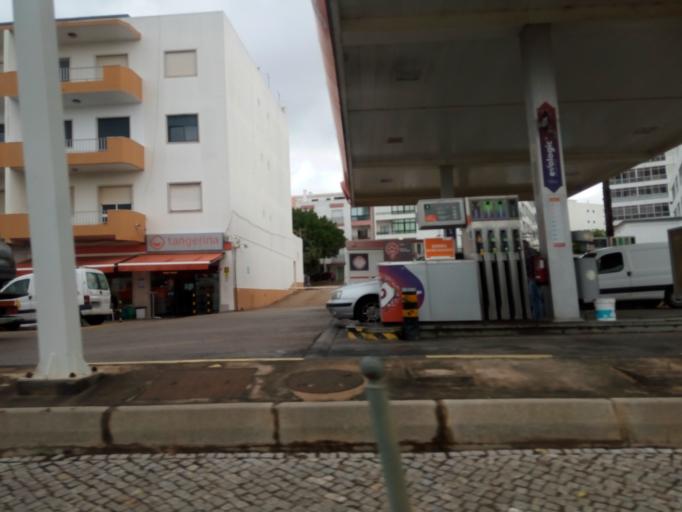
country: PT
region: Faro
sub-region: Loule
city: Loule
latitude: 37.1351
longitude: -8.0212
